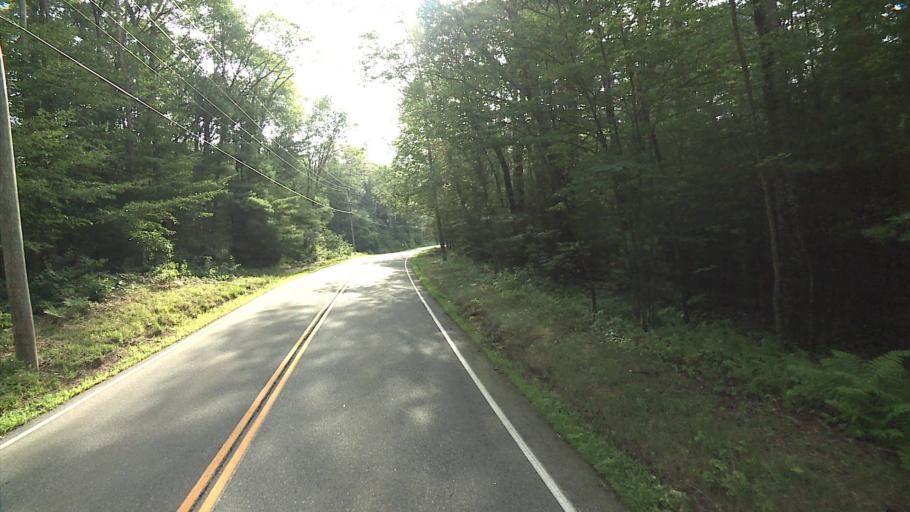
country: US
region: Massachusetts
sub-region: Hampden County
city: Holland
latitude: 41.9856
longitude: -72.0984
